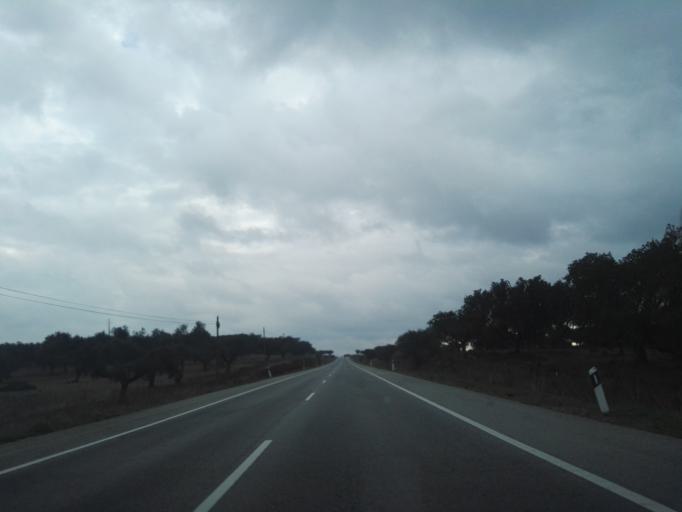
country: PT
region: Portalegre
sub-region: Arronches
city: Arronches
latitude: 39.1570
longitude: -7.3175
